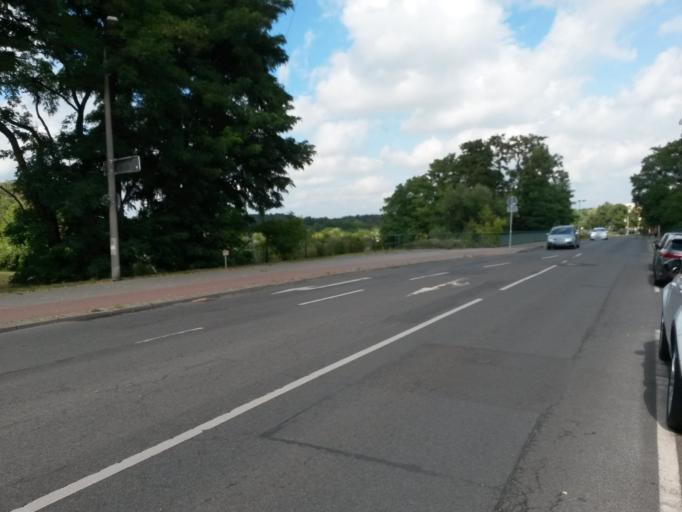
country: DE
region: Brandenburg
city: Eberswalde
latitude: 52.8364
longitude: 13.8084
